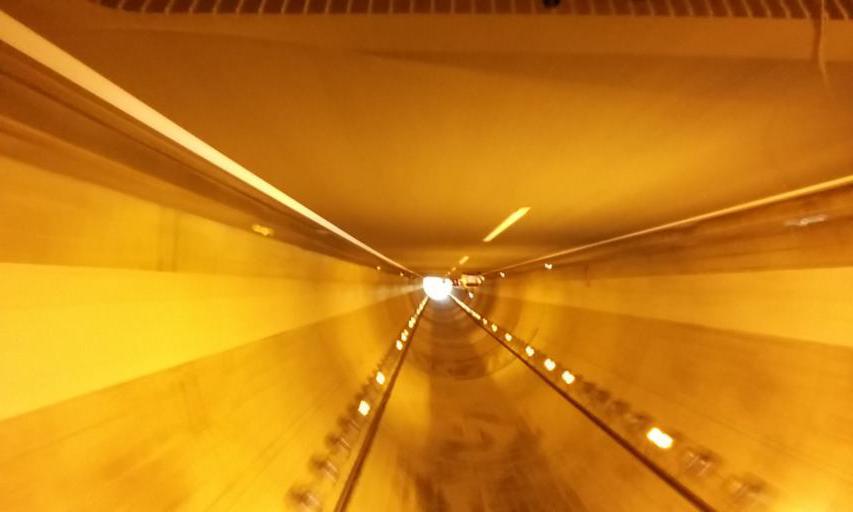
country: JP
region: Kyoto
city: Fukuchiyama
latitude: 35.1880
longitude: 135.1411
